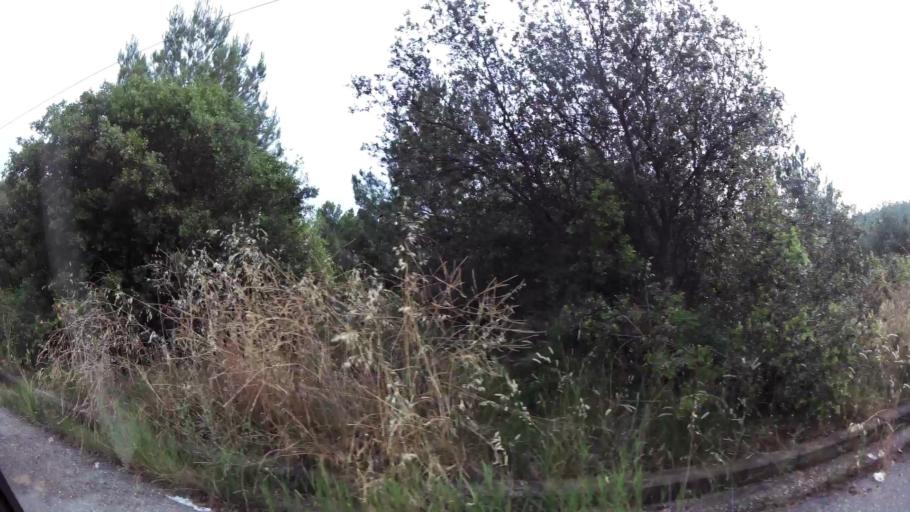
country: GR
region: Central Macedonia
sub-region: Nomos Thessalonikis
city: Oraiokastro
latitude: 40.7319
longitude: 22.9118
